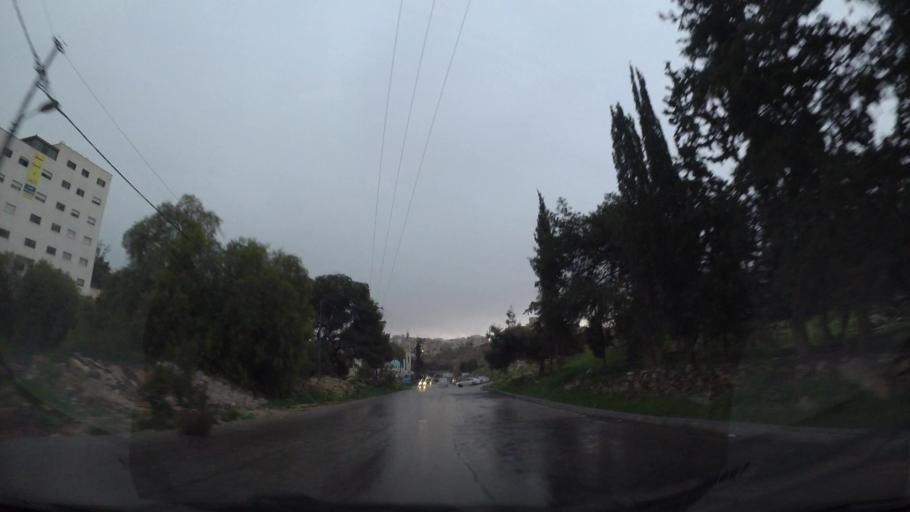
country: JO
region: Amman
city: Amman
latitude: 31.9914
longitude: 35.9751
